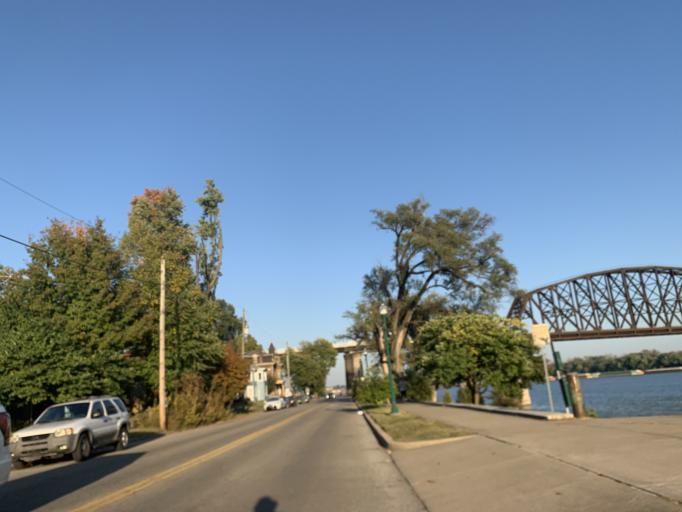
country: US
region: Indiana
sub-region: Clark County
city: Jeffersonville
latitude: 38.2681
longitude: -85.7432
